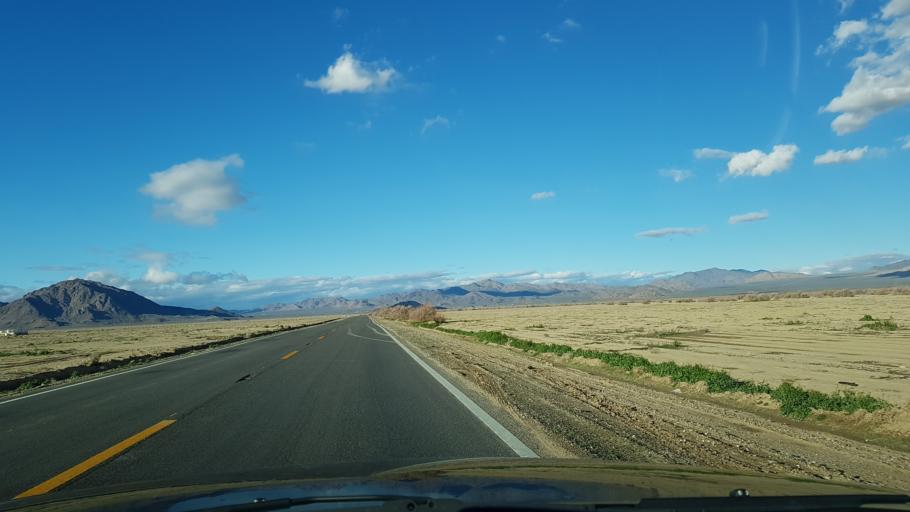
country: US
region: California
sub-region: San Bernardino County
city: Lucerne Valley
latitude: 34.4744
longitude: -116.9454
